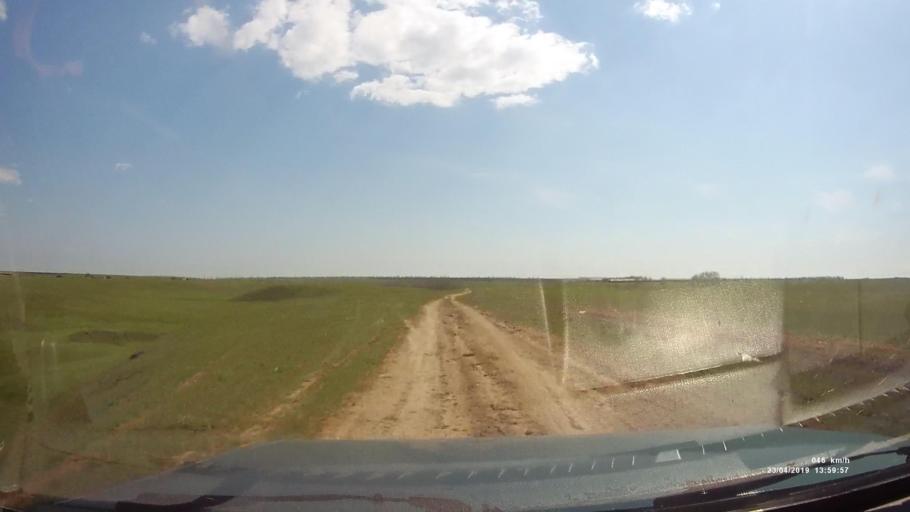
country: RU
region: Rostov
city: Remontnoye
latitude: 46.5630
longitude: 42.9468
